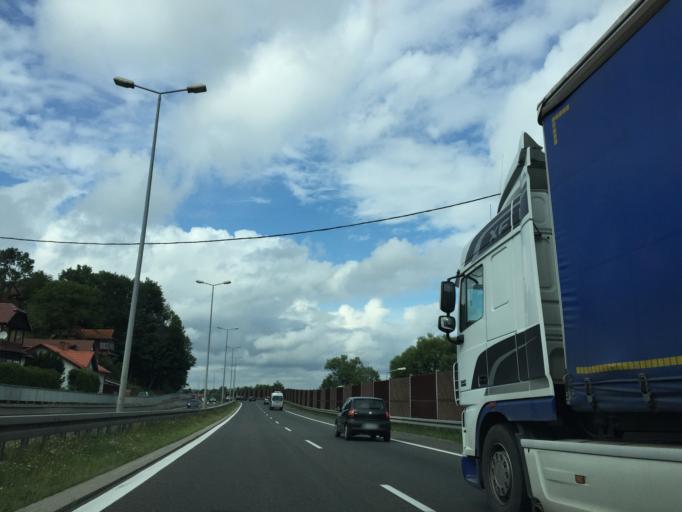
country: PL
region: Lesser Poland Voivodeship
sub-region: Powiat myslenicki
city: Myslenice
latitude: 49.8222
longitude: 19.9398
